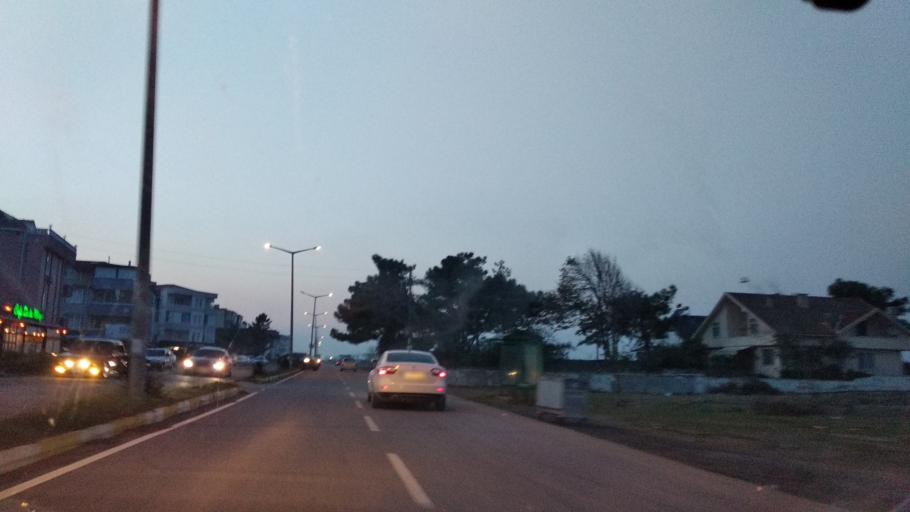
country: TR
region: Sakarya
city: Karasu
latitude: 41.0951
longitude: 30.7327
